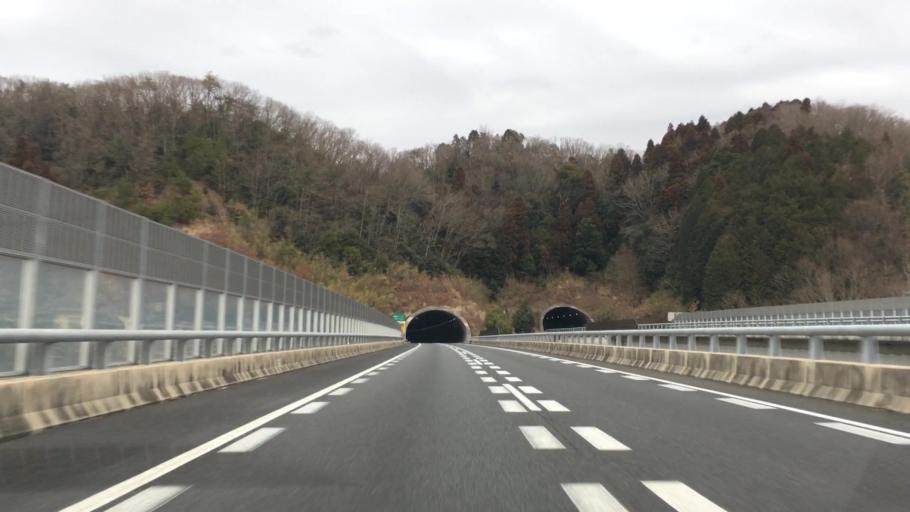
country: JP
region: Aichi
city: Seto
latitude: 35.2598
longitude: 137.1524
